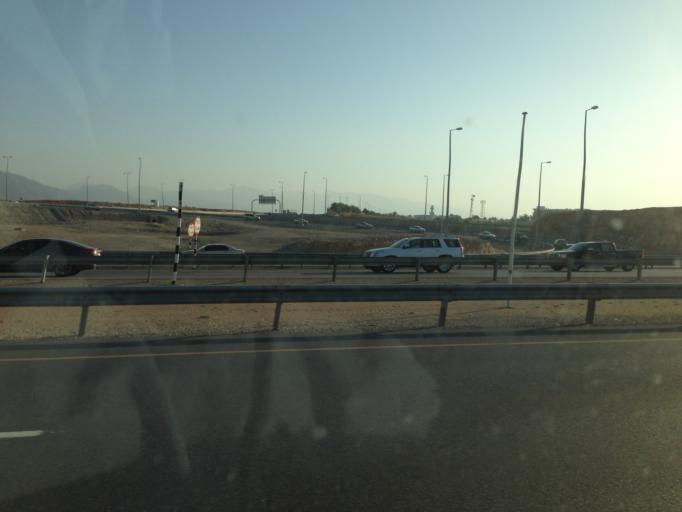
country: OM
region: Muhafazat Masqat
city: Bawshar
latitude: 23.5671
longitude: 58.3785
